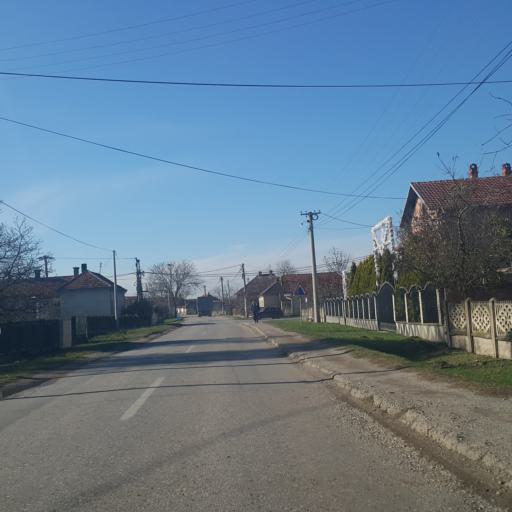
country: RS
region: Central Serbia
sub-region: Sumadijski Okrug
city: Lapovo
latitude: 44.2375
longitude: 21.1053
